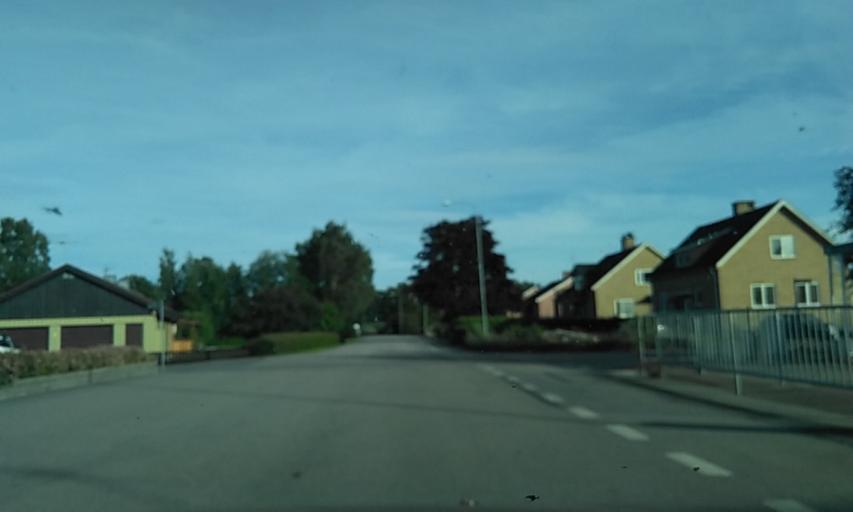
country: SE
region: Vaestra Goetaland
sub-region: Vara Kommun
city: Vara
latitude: 58.3233
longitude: 12.9272
